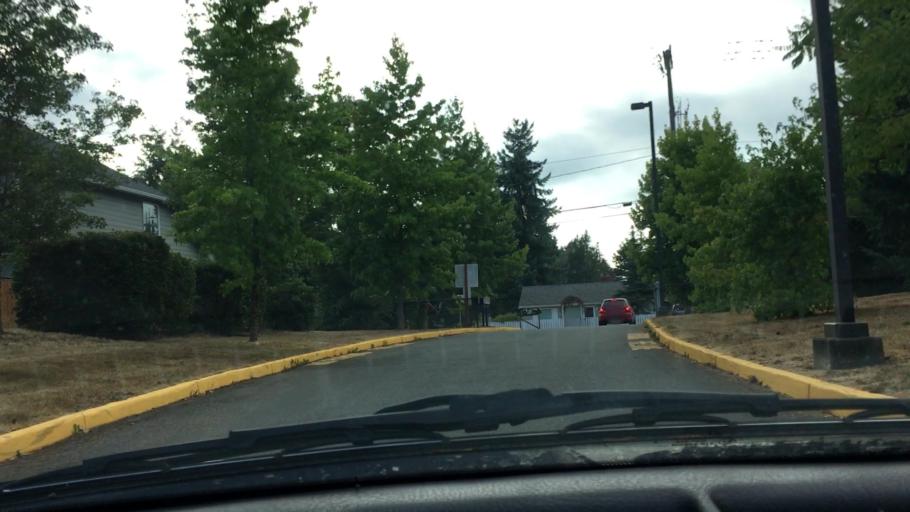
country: US
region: Washington
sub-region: King County
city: Burien
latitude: 47.4585
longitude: -122.3572
